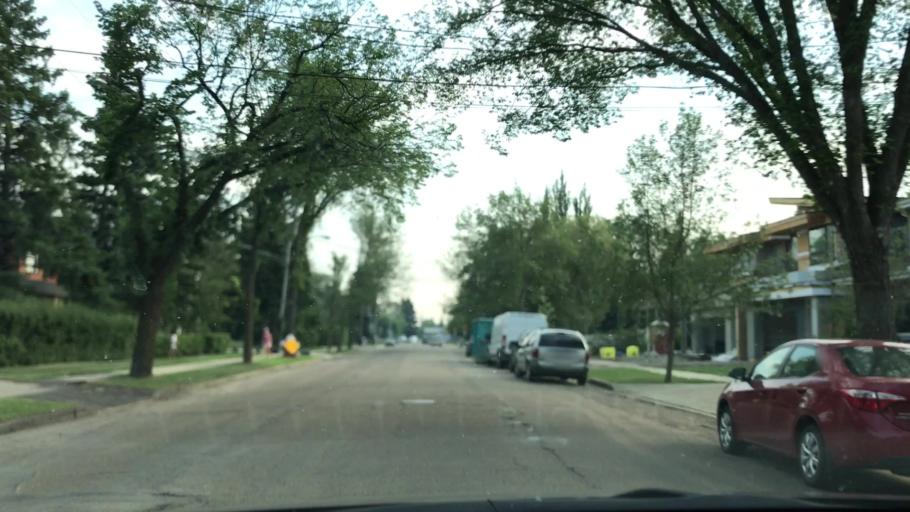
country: CA
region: Alberta
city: Edmonton
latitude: 53.4926
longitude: -113.5119
